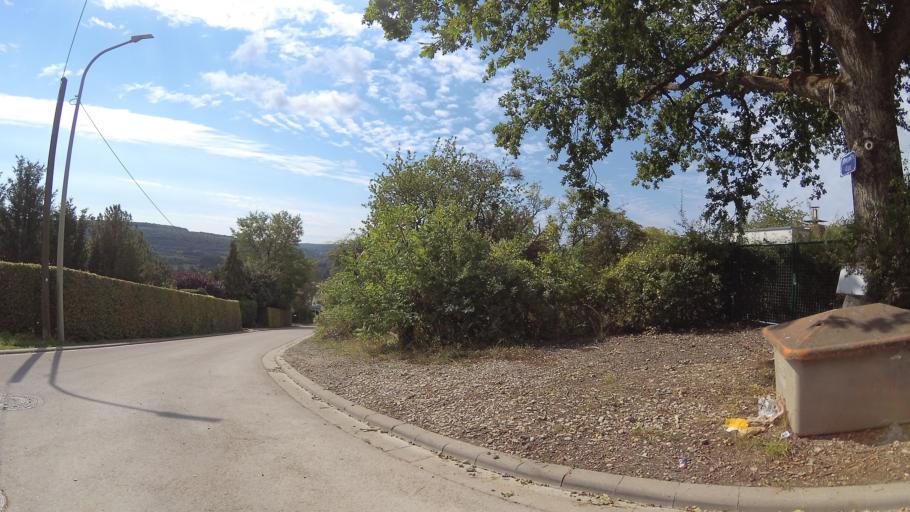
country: DE
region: Saarland
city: Gersheim
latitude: 49.1418
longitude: 7.1804
